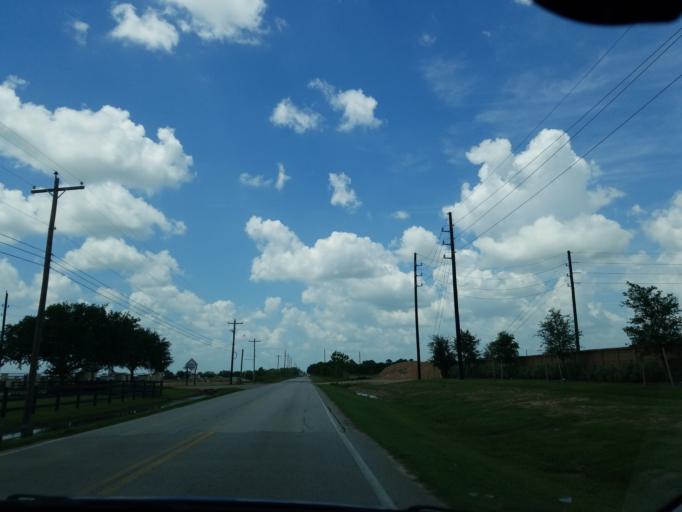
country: US
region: Texas
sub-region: Harris County
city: Katy
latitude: 29.8524
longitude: -95.8070
